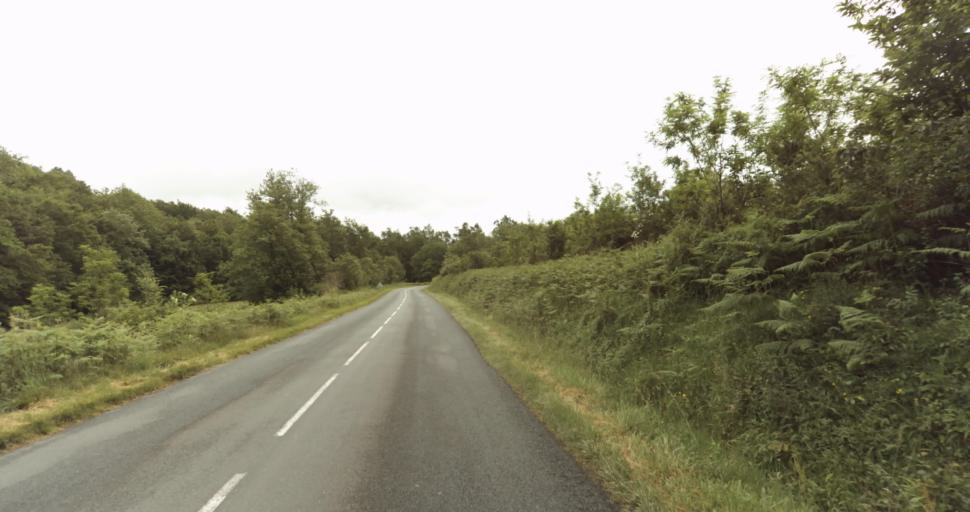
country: FR
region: Aquitaine
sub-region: Departement de la Dordogne
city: Belves
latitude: 44.7175
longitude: 0.9392
